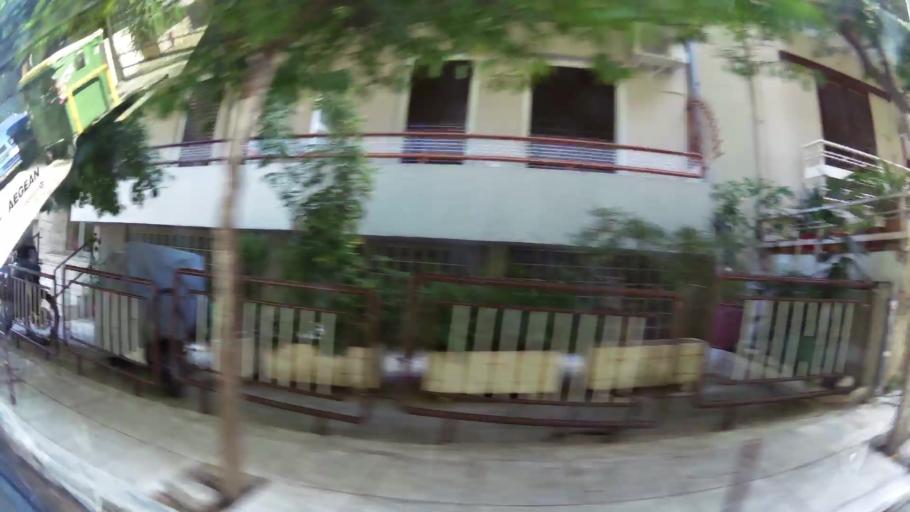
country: GR
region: Attica
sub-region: Nomarchia Athinas
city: Kaisariani
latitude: 37.9733
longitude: 23.7757
